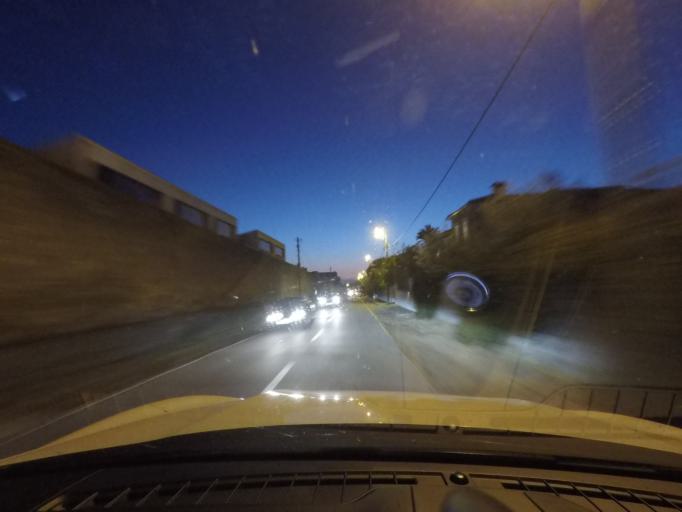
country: PT
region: Porto
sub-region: Vila Nova de Gaia
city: Arcozelo
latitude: 41.0405
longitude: -8.6426
